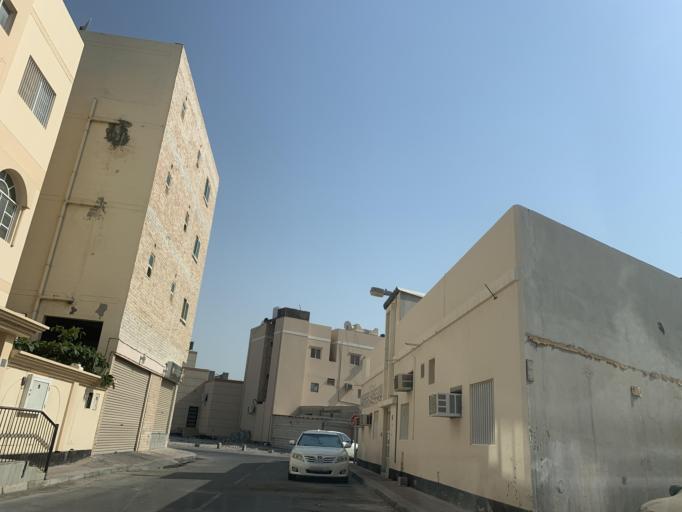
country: BH
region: Manama
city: Jidd Hafs
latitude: 26.2053
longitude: 50.5320
